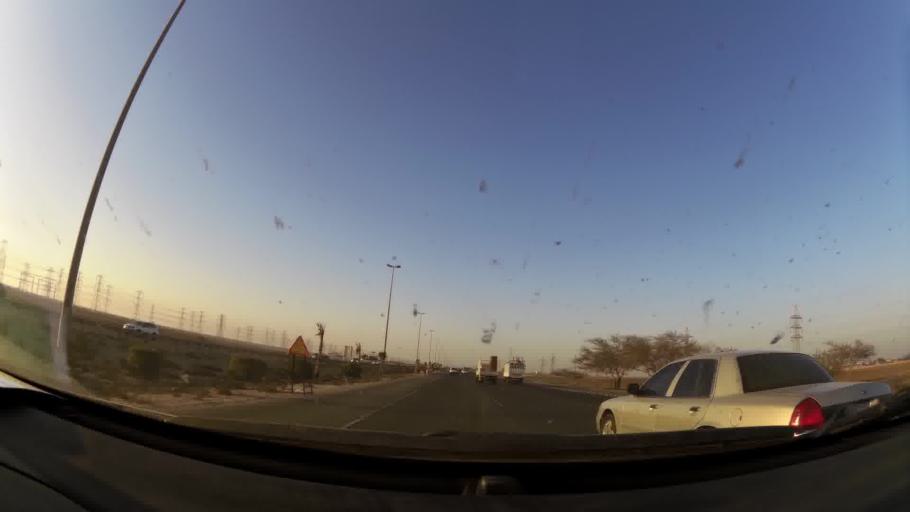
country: KW
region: Al Ahmadi
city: Al Fahahil
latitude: 28.8009
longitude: 48.2703
